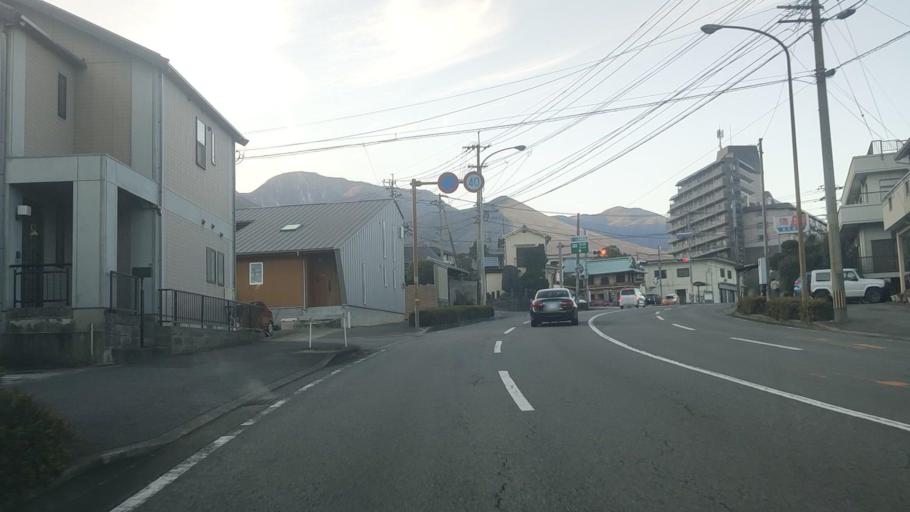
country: JP
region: Oita
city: Beppu
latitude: 33.2863
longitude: 131.4744
